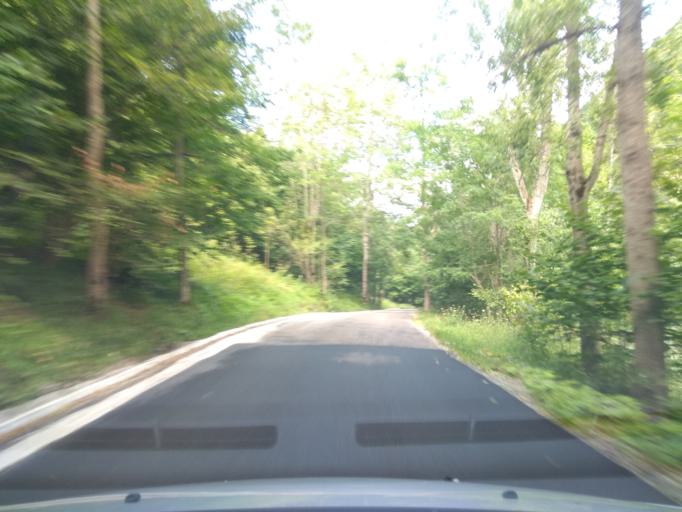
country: ES
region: Catalonia
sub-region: Provincia de Lleida
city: Vielha
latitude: 42.7123
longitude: 0.7195
